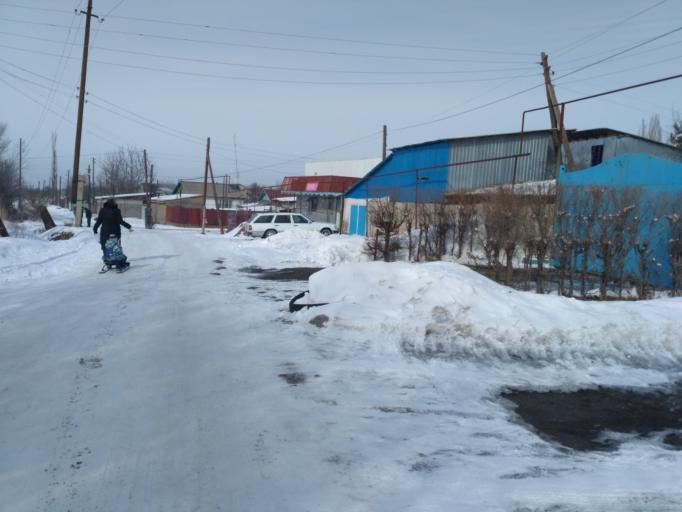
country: KZ
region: Almaty Oblysy
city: Burunday
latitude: 43.1588
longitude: 76.4023
